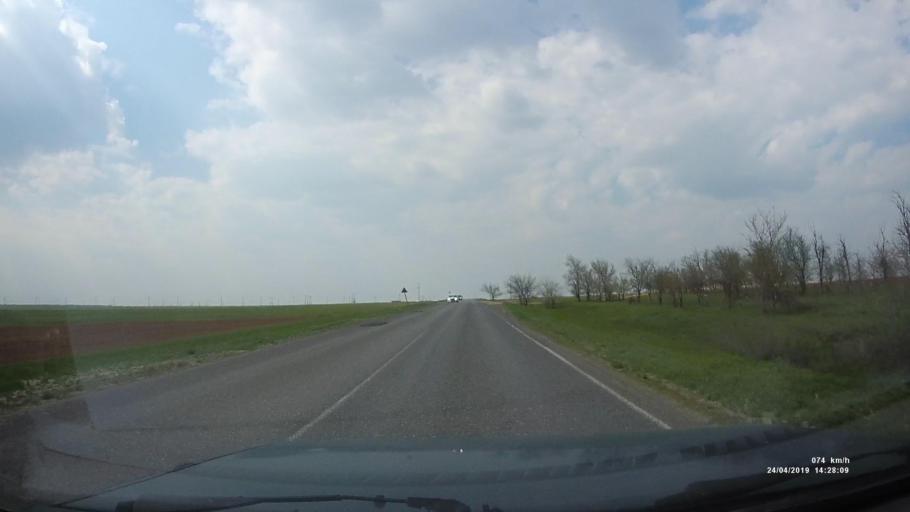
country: RU
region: Kalmykiya
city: Arshan'
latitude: 46.3367
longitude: 44.0331
